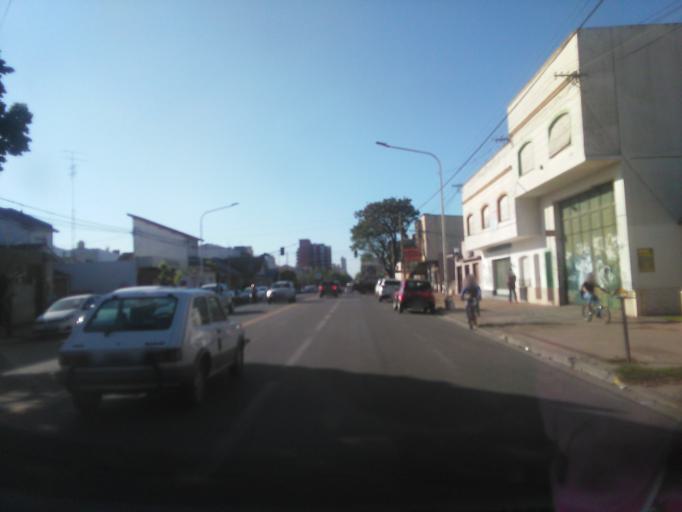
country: AR
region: Buenos Aires
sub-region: Partido de Tandil
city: Tandil
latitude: -37.3308
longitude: -59.1266
